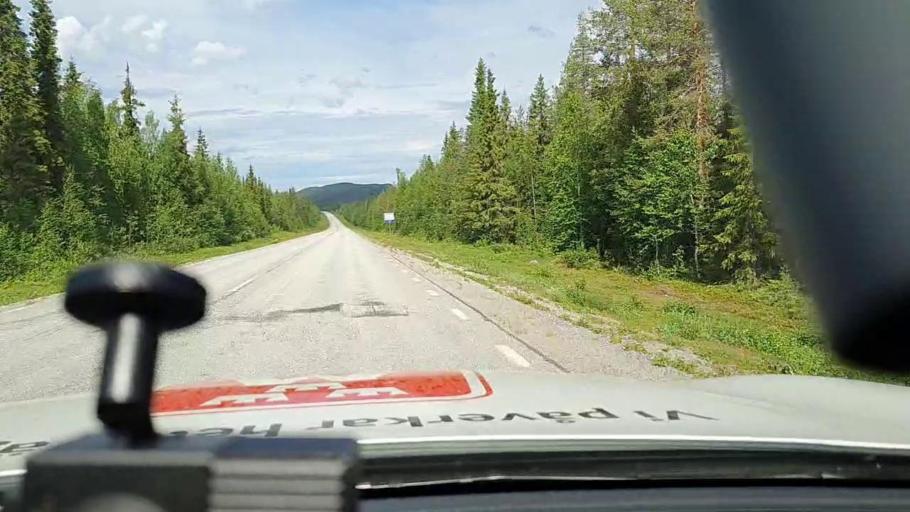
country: SE
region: Norrbotten
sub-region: Jokkmokks Kommun
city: Jokkmokk
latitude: 66.5459
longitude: 20.1335
